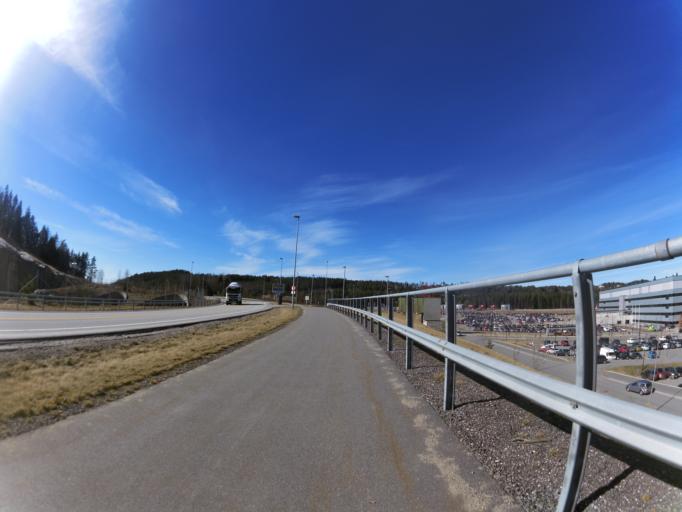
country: NO
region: Ostfold
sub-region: Sarpsborg
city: Sarpsborg
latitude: 59.3162
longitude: 11.0267
